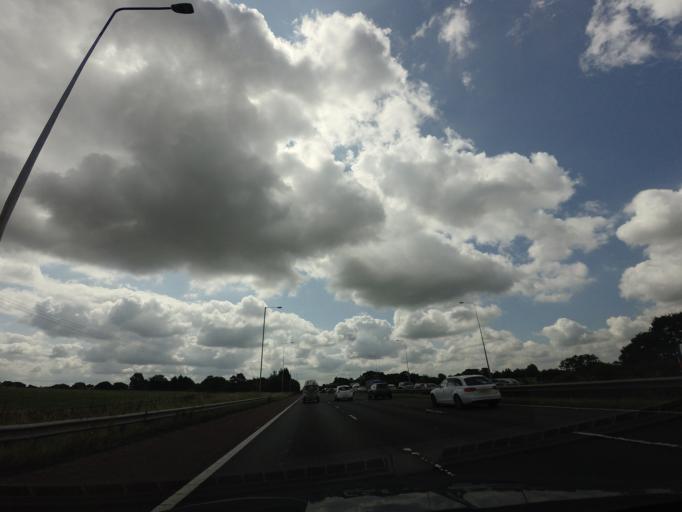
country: GB
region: England
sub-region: Borough of Wigan
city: Shevington
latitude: 53.5995
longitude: -2.6918
